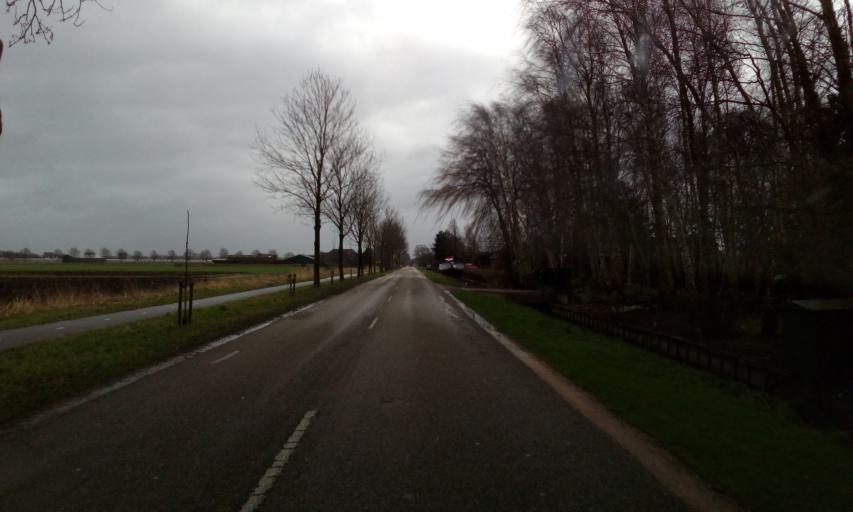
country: NL
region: North Holland
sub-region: Gemeente Uithoorn
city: Uithoorn
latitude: 52.2118
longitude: 4.8308
